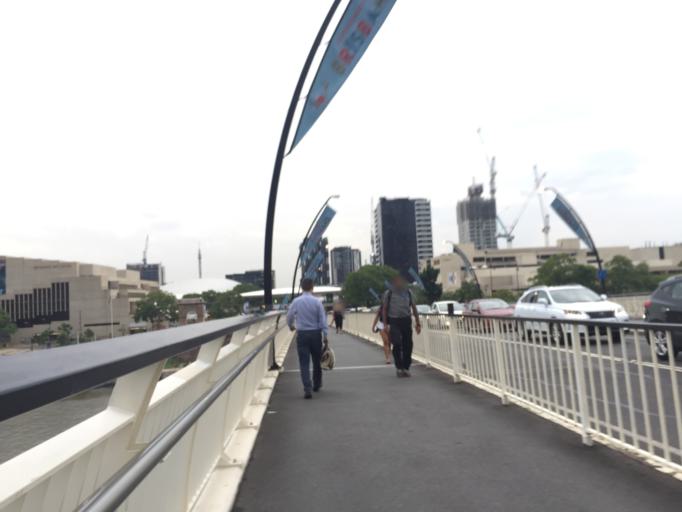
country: AU
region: Queensland
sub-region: Brisbane
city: South Brisbane
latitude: -27.4725
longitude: 153.0211
